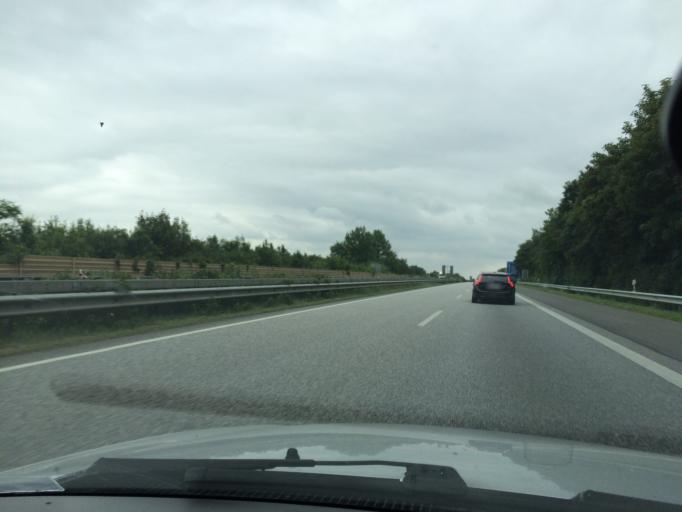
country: DE
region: Schleswig-Holstein
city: Jarplund-Weding
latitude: 54.7441
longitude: 9.3800
